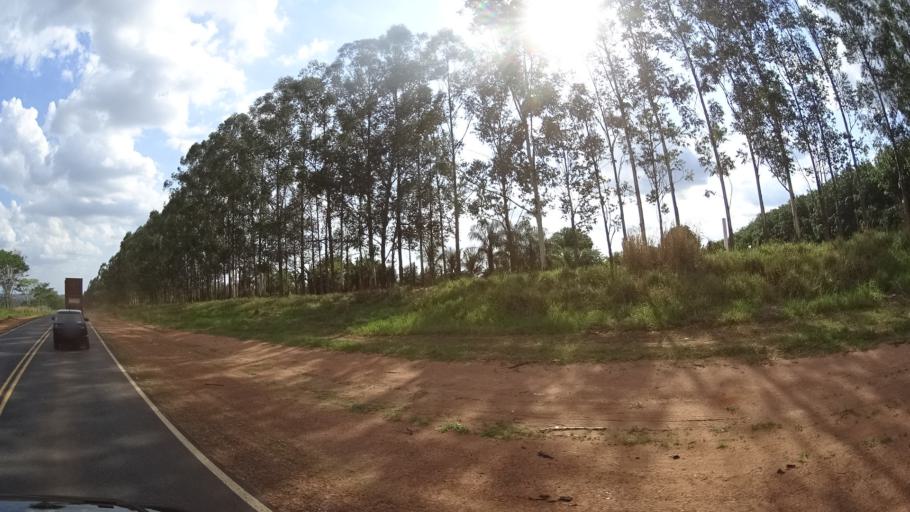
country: BR
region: Sao Paulo
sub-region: Urupes
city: Urupes
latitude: -21.1723
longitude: -49.2901
